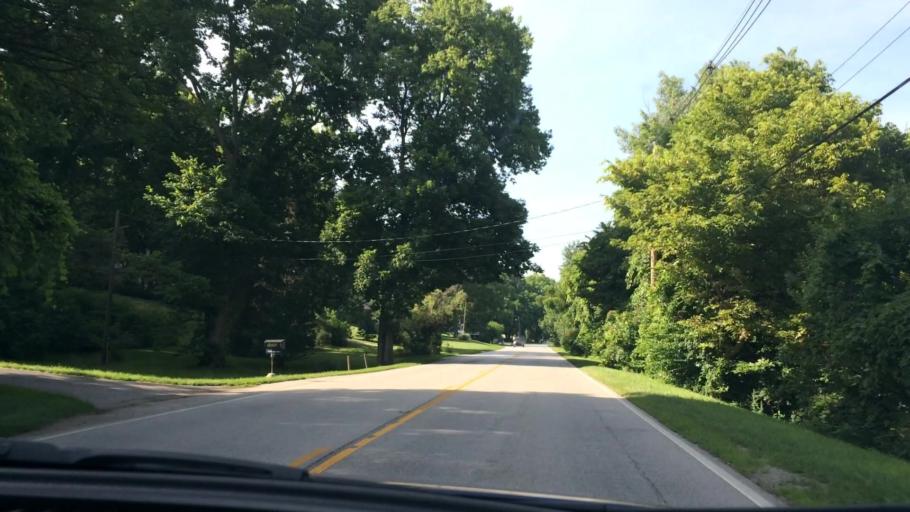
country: US
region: Indiana
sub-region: Tippecanoe County
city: West Lafayette
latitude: 40.4413
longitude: -86.8970
